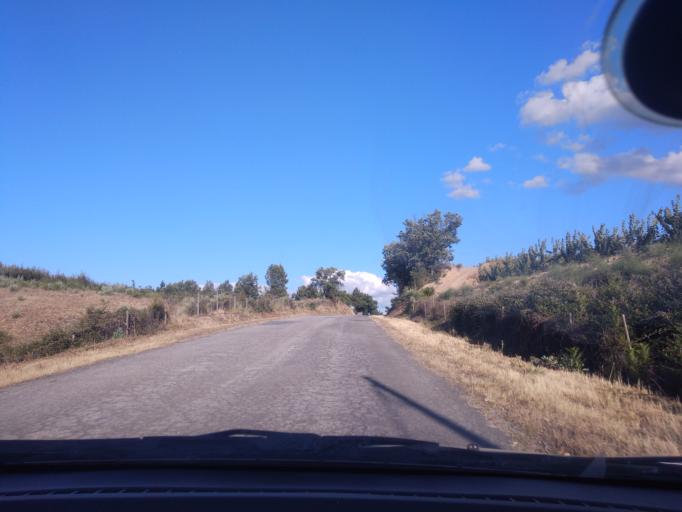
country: PT
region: Castelo Branco
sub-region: Covilha
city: Teixoso
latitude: 40.2362
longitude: -7.3834
